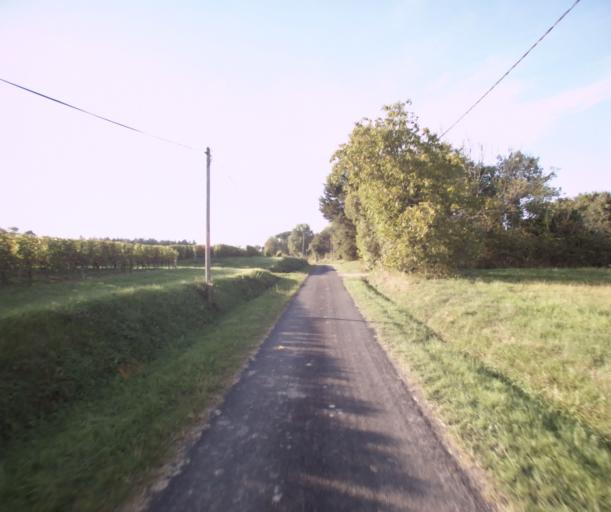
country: FR
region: Midi-Pyrenees
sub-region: Departement du Gers
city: Eauze
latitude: 43.8561
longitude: 0.0148
